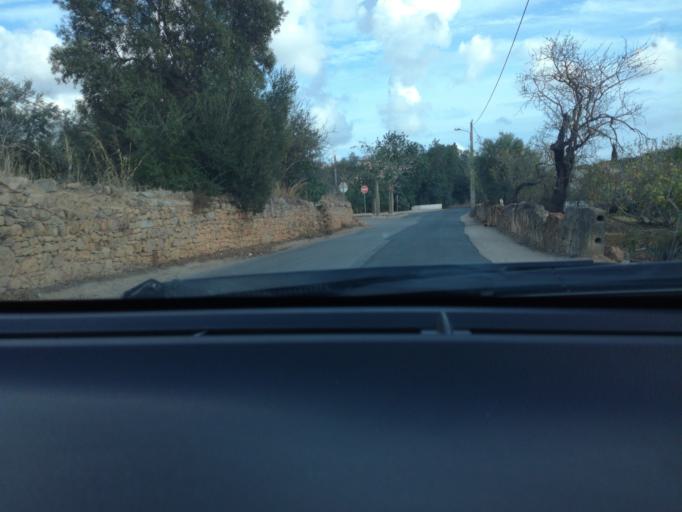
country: PT
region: Faro
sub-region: Sao Bras de Alportel
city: Sao Bras de Alportel
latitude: 37.0916
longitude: -7.8921
